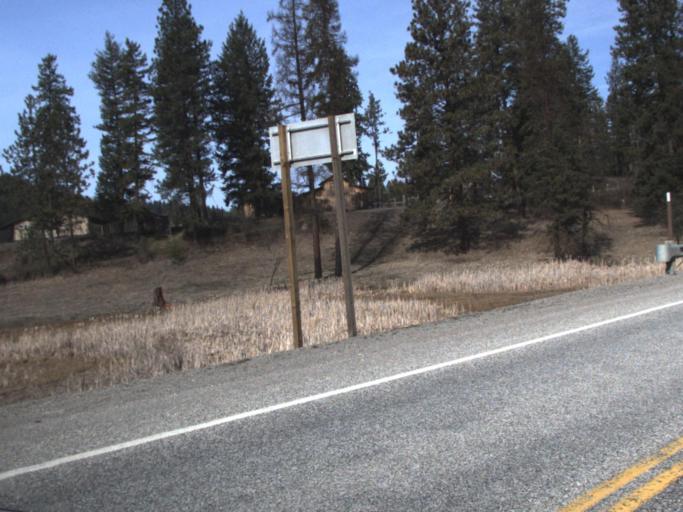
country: US
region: Washington
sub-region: Stevens County
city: Colville
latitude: 48.5162
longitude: -117.8068
